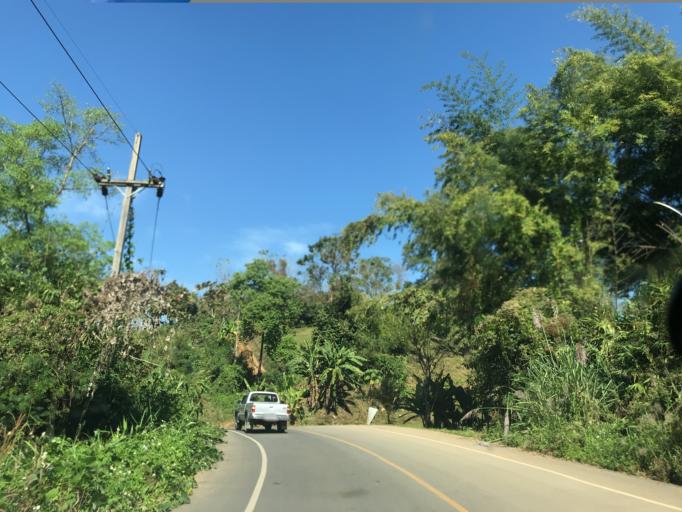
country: TH
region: Chiang Rai
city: Mae Lao
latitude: 19.8088
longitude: 99.6464
